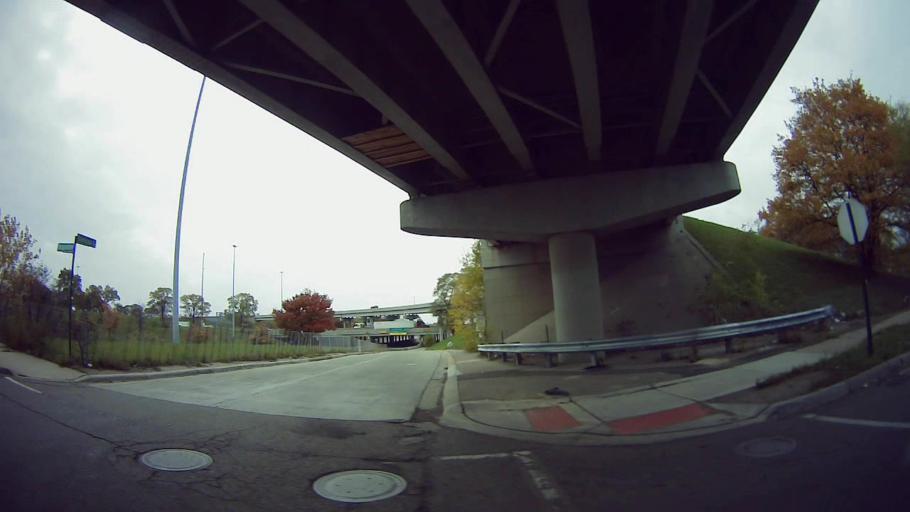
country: US
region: Michigan
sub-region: Wayne County
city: Highland Park
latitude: 42.4115
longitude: -83.0788
